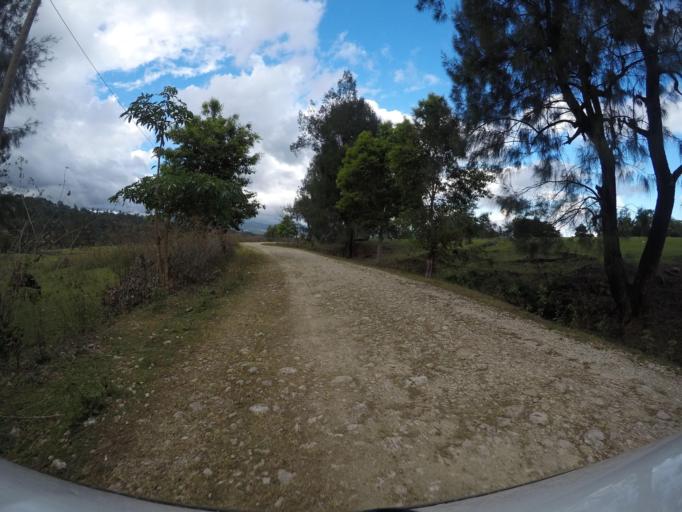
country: TL
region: Baucau
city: Venilale
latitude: -8.6808
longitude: 126.6449
